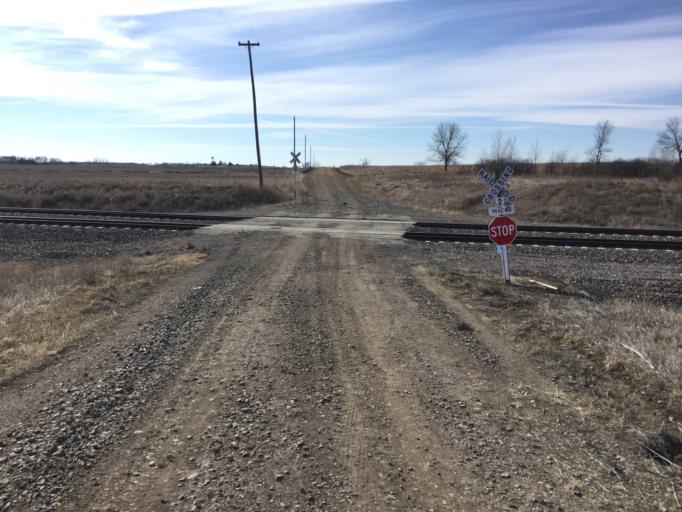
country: US
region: Kansas
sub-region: Marshall County
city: Marysville
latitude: 39.8955
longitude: -96.7500
